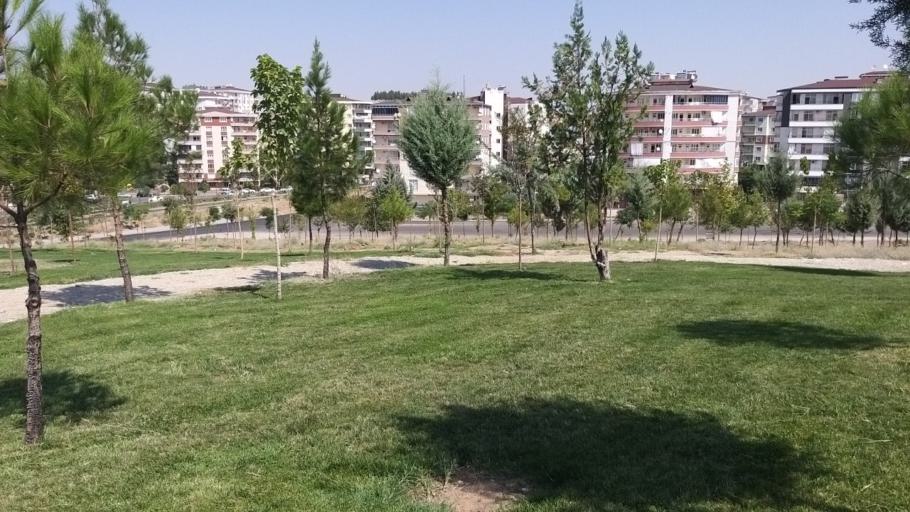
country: TR
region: Batman
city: Demiryol
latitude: 37.9074
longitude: 41.1454
